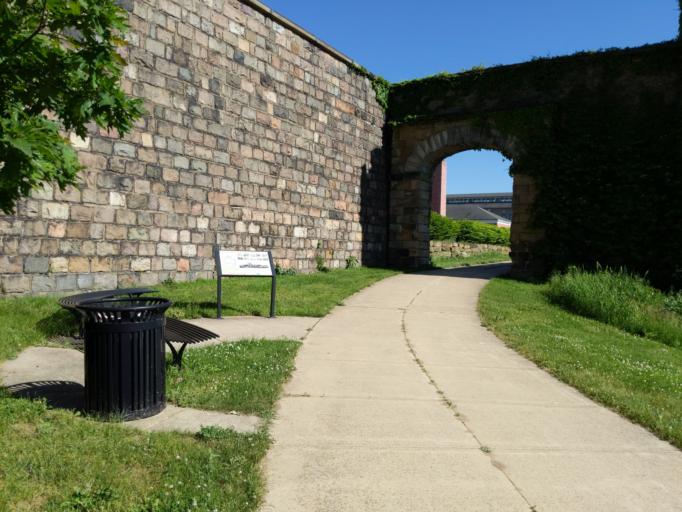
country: US
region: Michigan
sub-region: Jackson County
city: Jackson
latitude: 42.2587
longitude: -84.4073
